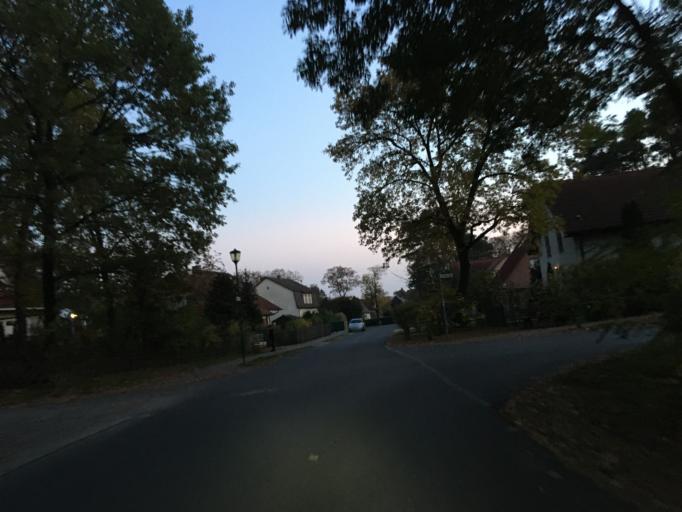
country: DE
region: Brandenburg
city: Glienicke
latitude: 52.6737
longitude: 13.3244
